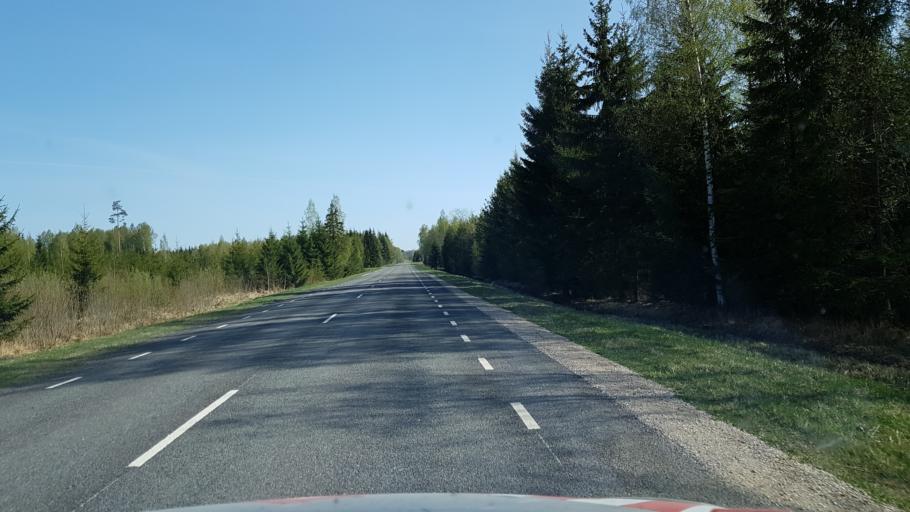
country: EE
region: Viljandimaa
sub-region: Karksi vald
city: Karksi-Nuia
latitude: 58.2243
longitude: 25.5719
